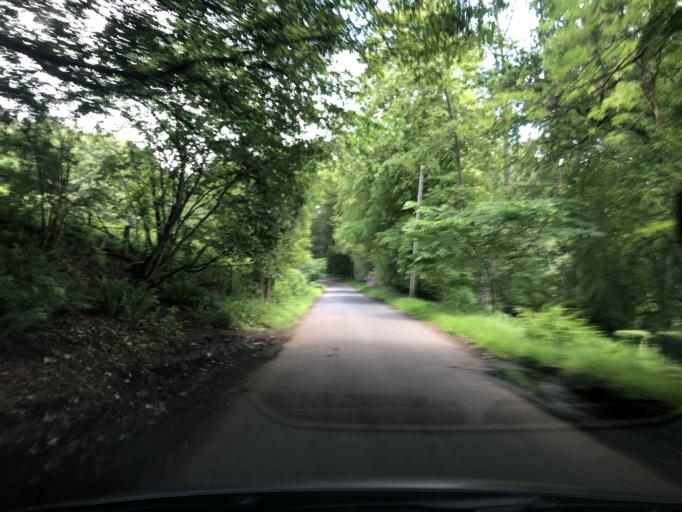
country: GB
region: Scotland
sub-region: Angus
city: Kirriemuir
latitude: 56.7249
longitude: -2.9812
